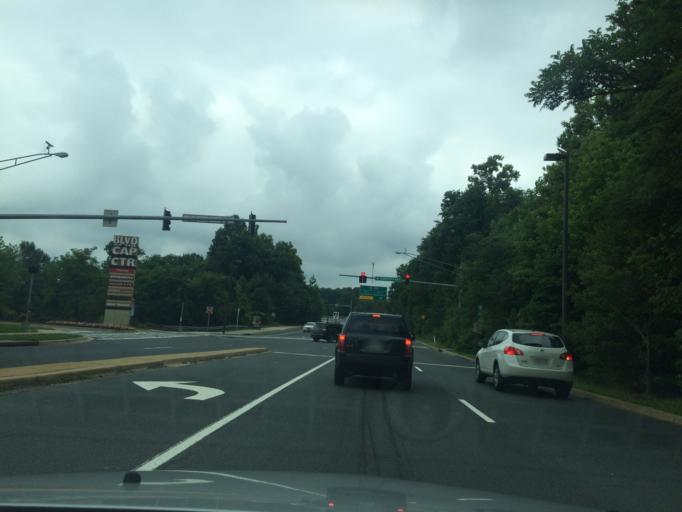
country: US
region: Maryland
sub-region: Prince George's County
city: Lake Arbor
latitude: 38.9053
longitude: -76.8463
